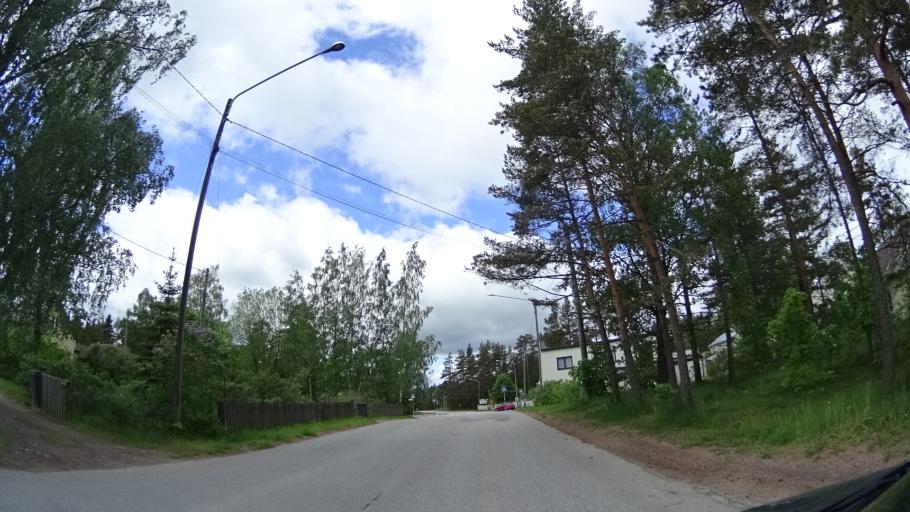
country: FI
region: Uusimaa
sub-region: Raaseporin
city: Inga
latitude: 60.1372
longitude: 23.8649
